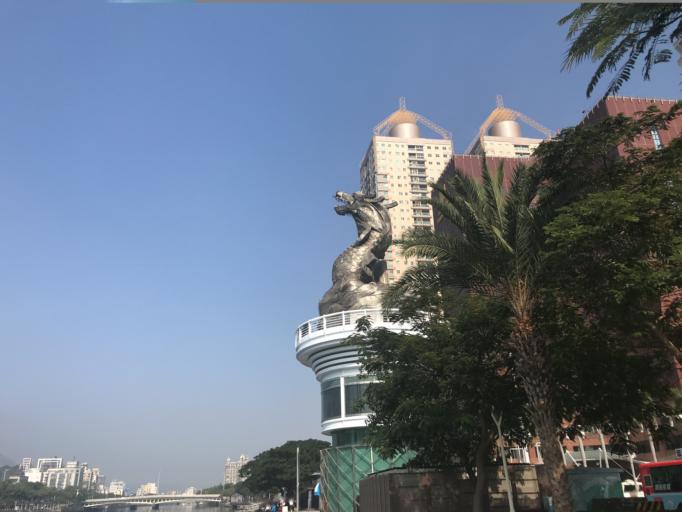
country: TW
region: Kaohsiung
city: Kaohsiung
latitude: 22.6232
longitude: 120.2904
